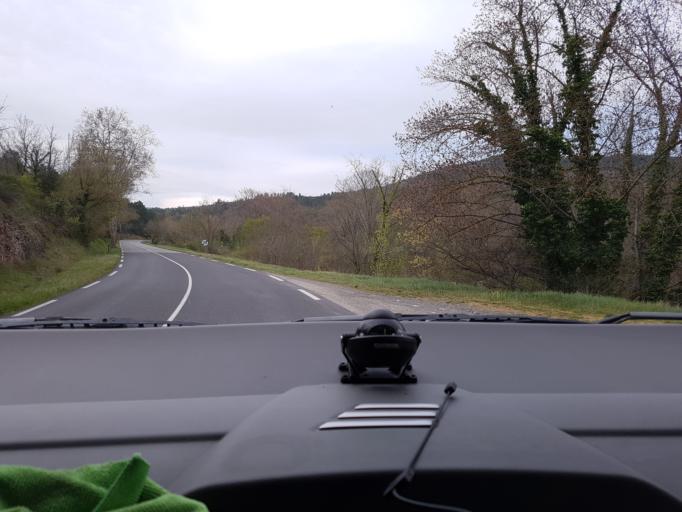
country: FR
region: Languedoc-Roussillon
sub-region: Departement de l'Aude
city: Couiza
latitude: 42.9666
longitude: 2.2596
